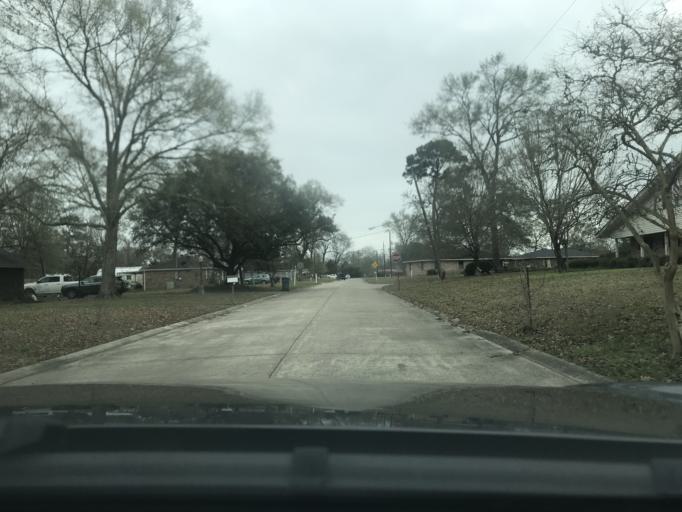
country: US
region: Louisiana
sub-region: Calcasieu Parish
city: Westlake
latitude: 30.2557
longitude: -93.2544
